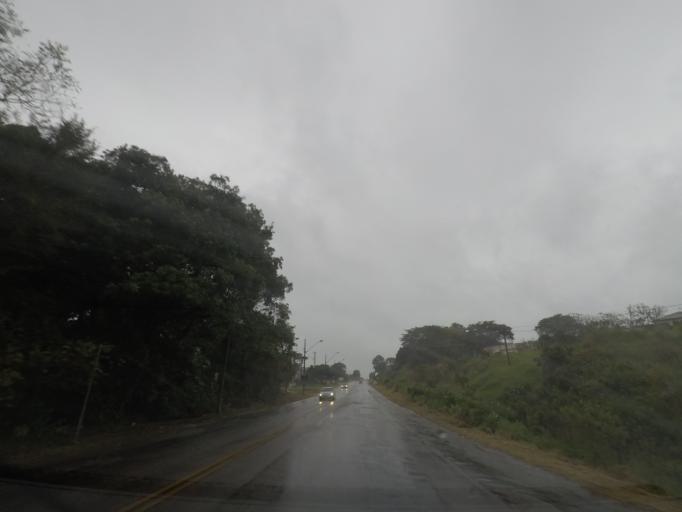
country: BR
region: Parana
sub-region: Almirante Tamandare
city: Almirante Tamandare
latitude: -25.3650
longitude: -49.2777
